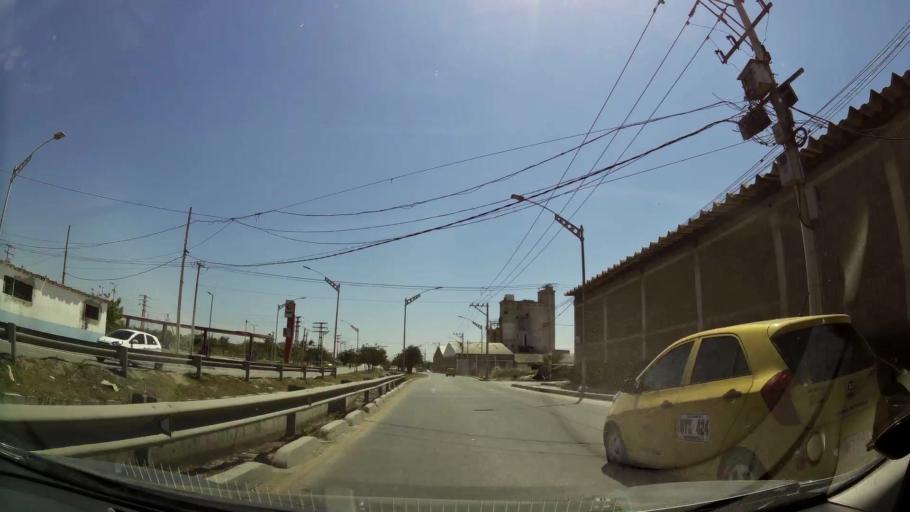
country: CO
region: Atlantico
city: Barranquilla
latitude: 10.9807
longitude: -74.7697
